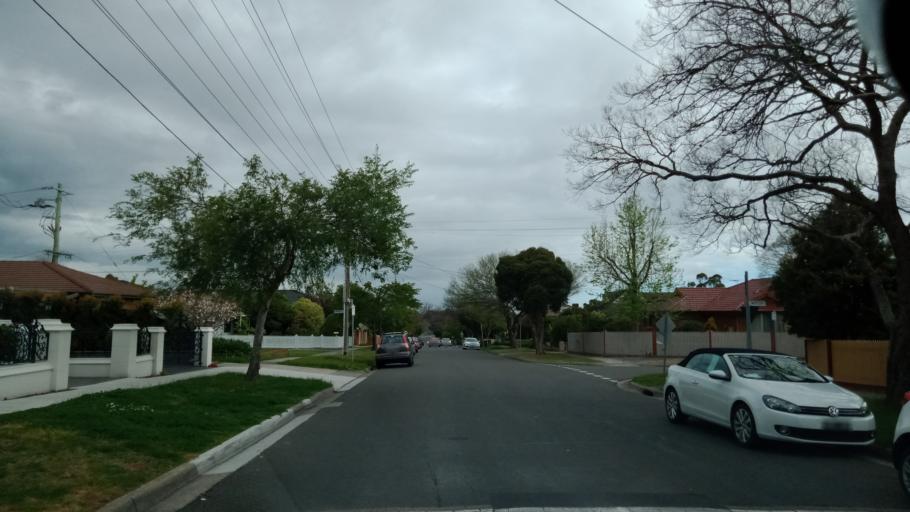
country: AU
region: Victoria
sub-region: Monash
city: Notting Hill
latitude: -37.8832
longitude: 145.1604
